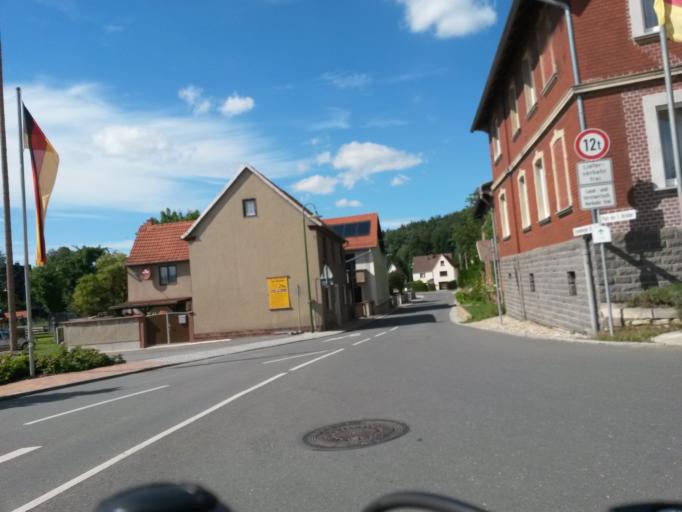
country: DE
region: Thuringia
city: Weissenborn
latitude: 50.9234
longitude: 11.8822
